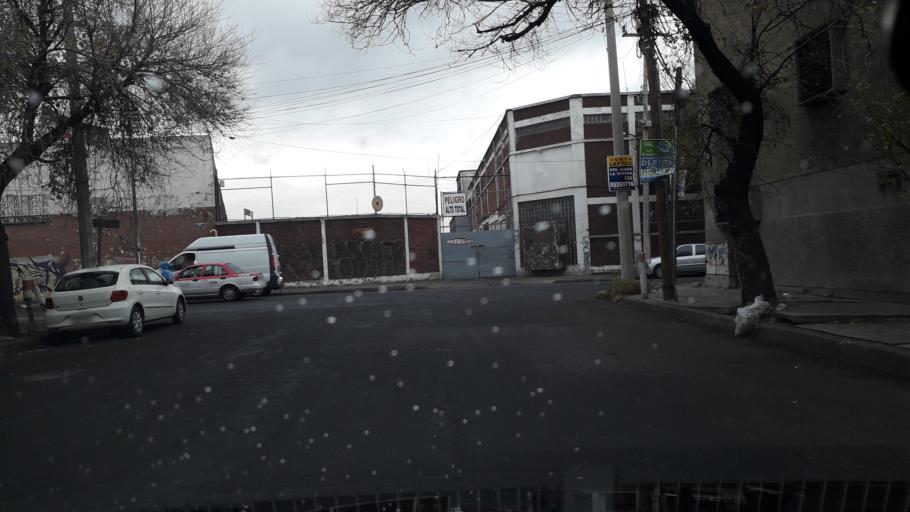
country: MX
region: Mexico City
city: Cuauhtemoc
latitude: 19.4609
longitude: -99.1538
